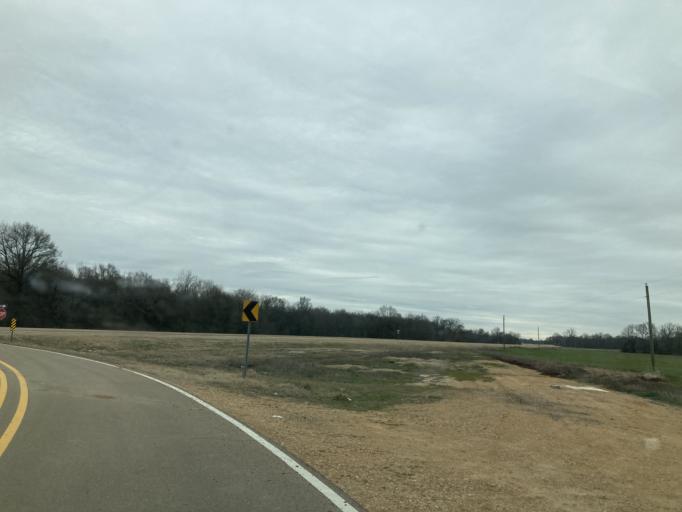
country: US
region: Mississippi
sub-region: Yazoo County
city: Yazoo City
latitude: 33.0096
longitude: -90.4703
